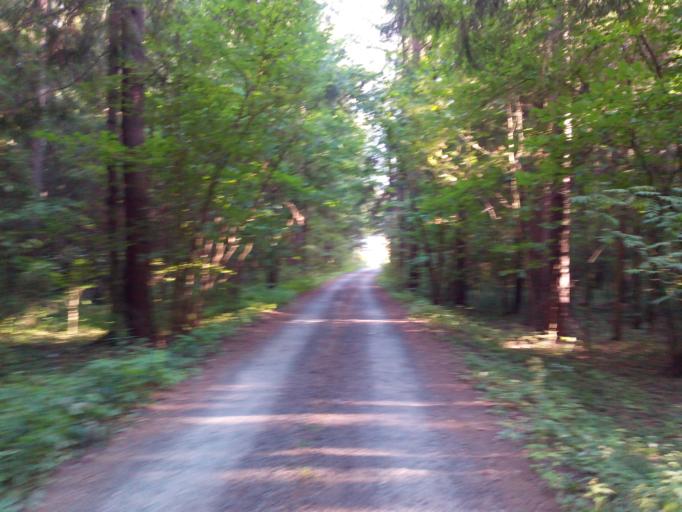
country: RU
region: Moskovskaya
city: Ruza
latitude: 55.5265
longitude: 36.1989
